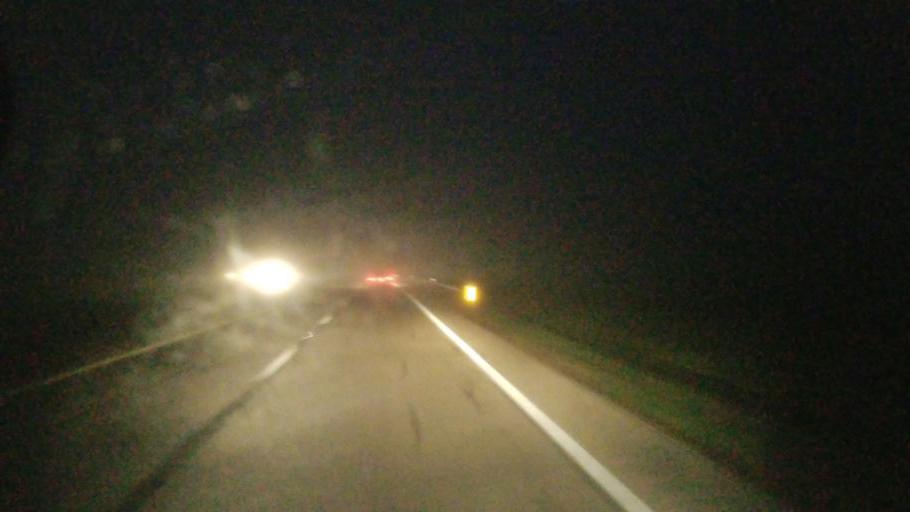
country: US
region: Ohio
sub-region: Ross County
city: Kingston
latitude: 39.5001
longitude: -82.9744
